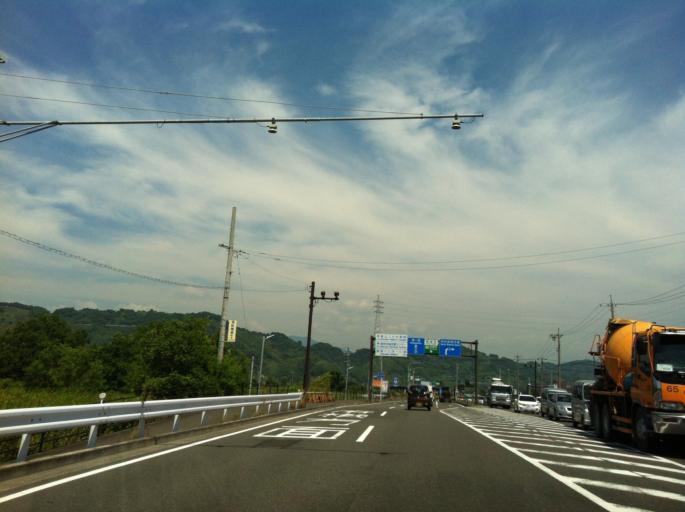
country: JP
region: Shizuoka
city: Shizuoka-shi
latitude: 35.0109
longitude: 138.4002
